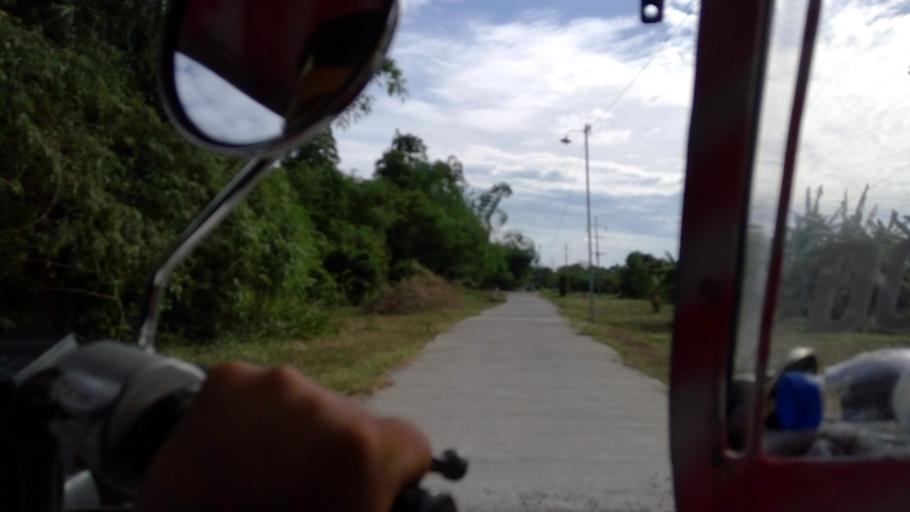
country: PH
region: Ilocos
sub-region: Province of La Union
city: San Eugenio
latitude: 16.3693
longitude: 120.3524
